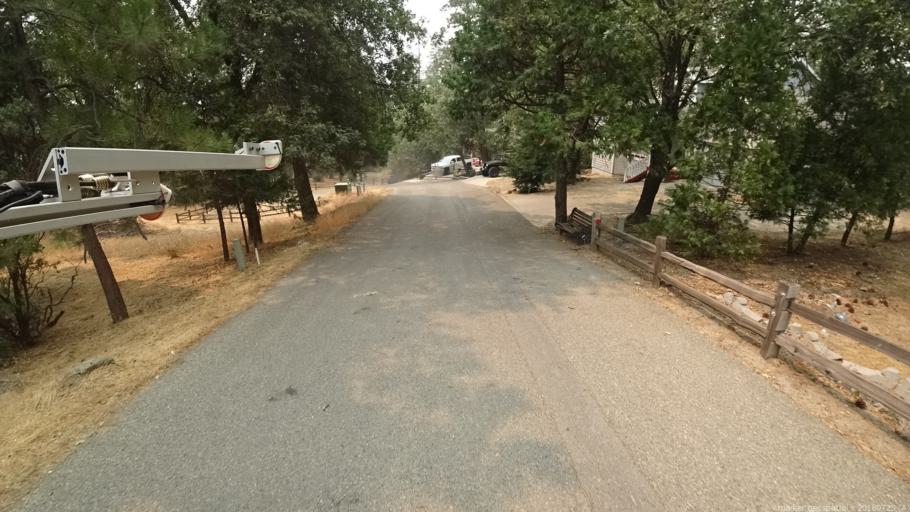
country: US
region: California
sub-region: Madera County
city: Oakhurst
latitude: 37.3215
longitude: -119.5507
